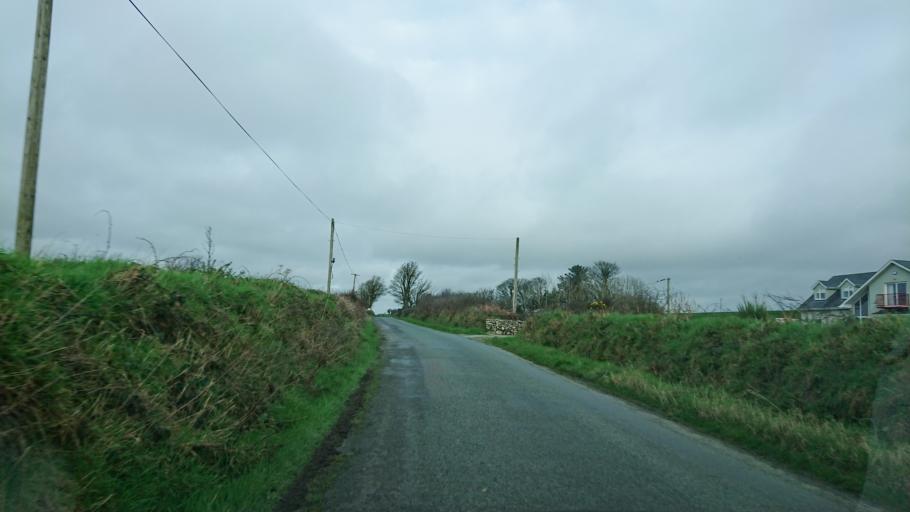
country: IE
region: Munster
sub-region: Waterford
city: Portlaw
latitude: 52.1749
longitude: -7.3043
